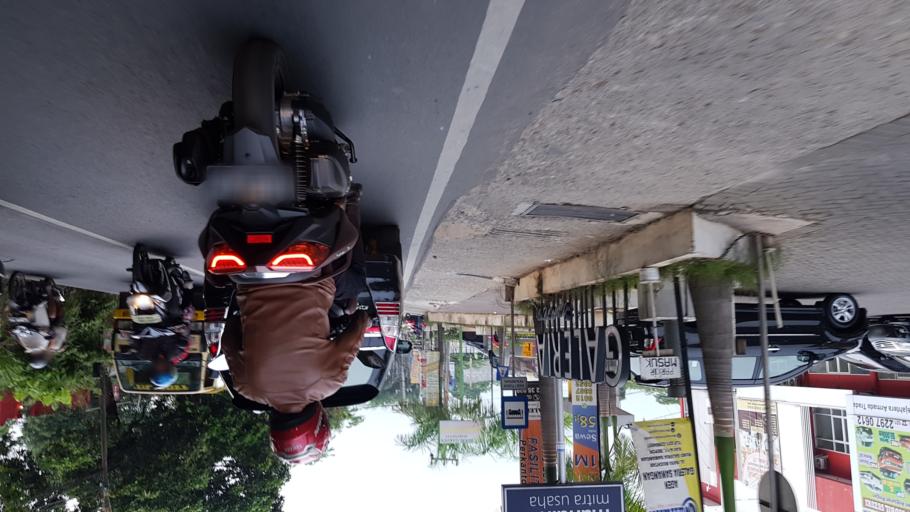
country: ID
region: West Java
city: Sawangan
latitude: -6.3957
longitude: 106.7724
